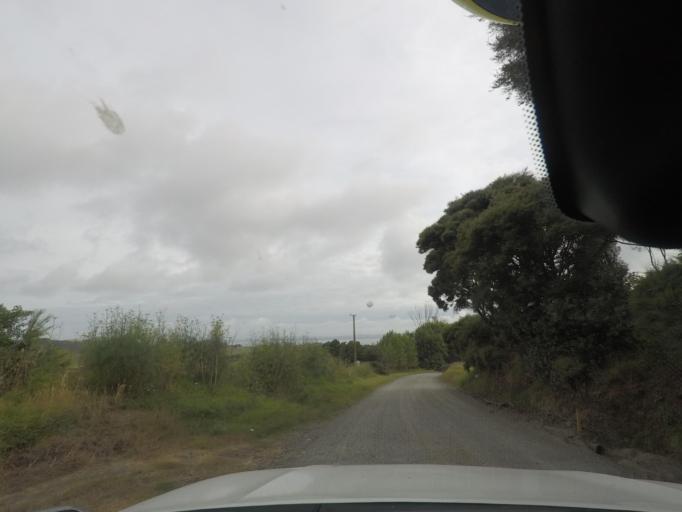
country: NZ
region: Auckland
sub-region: Auckland
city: Parakai
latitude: -36.4773
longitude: 174.2562
